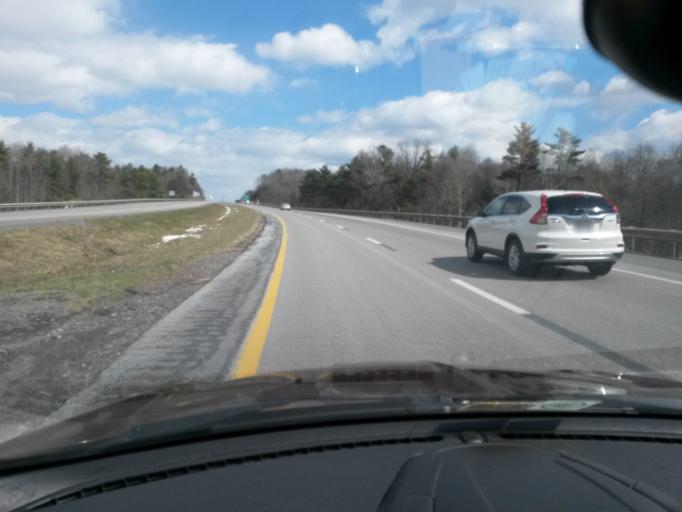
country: US
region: West Virginia
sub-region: Raleigh County
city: Shady Spring
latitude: 37.7651
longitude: -81.0319
